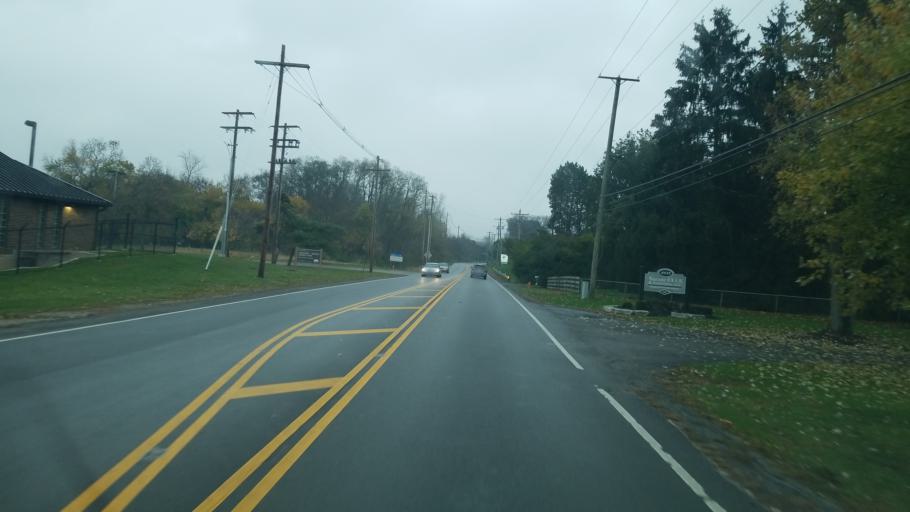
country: US
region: Ohio
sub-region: Franklin County
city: Worthington
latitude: 40.0616
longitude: -83.0366
